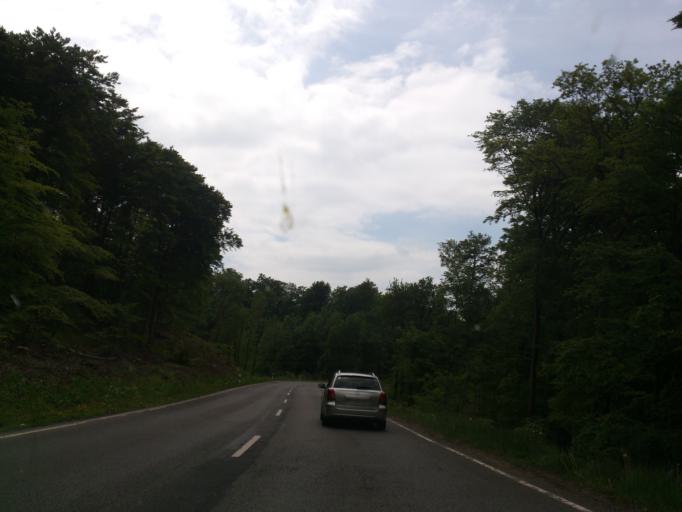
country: DE
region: Hesse
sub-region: Regierungsbezirk Kassel
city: Calden
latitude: 51.3497
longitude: 9.3914
